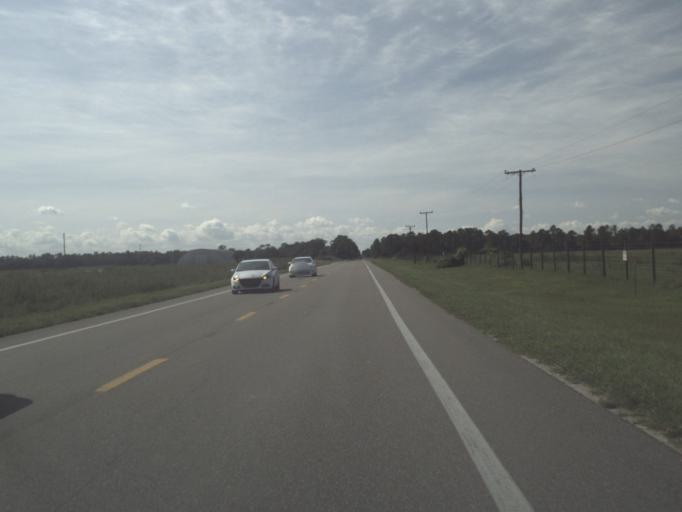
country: US
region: Florida
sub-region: DeSoto County
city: Nocatee
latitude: 26.9811
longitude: -81.7606
